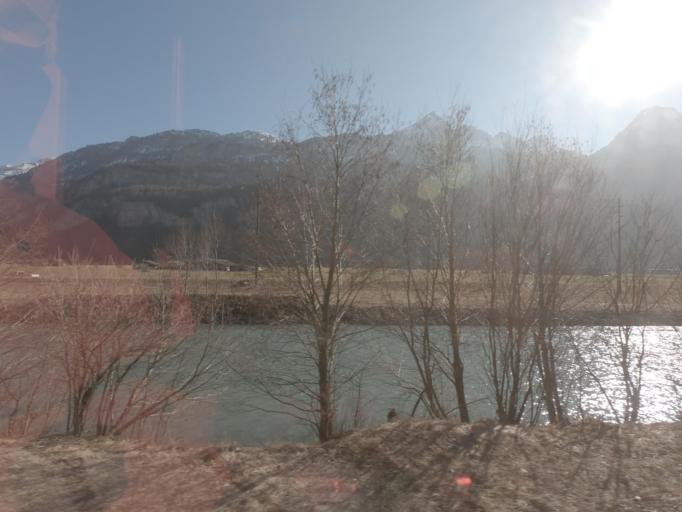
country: CH
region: Obwalden
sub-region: Obwalden
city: Lungern
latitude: 46.7444
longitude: 8.1310
